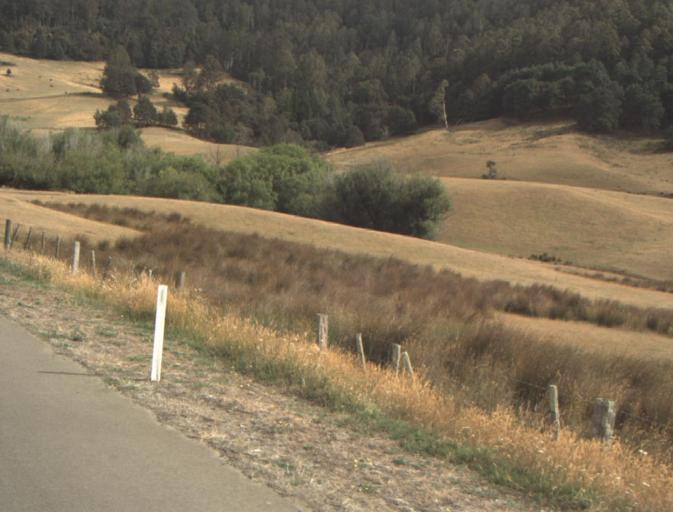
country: AU
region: Tasmania
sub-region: Dorset
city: Scottsdale
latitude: -41.4500
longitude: 147.5896
